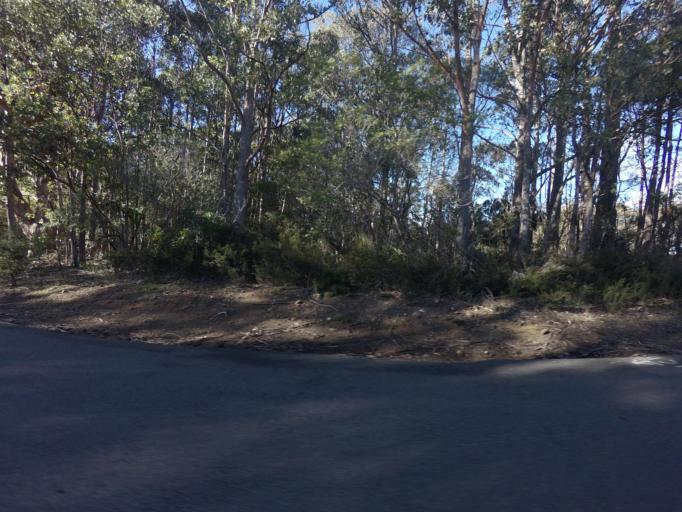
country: AU
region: Tasmania
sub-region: Glenorchy
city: Berriedale
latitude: -42.8380
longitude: 147.1586
